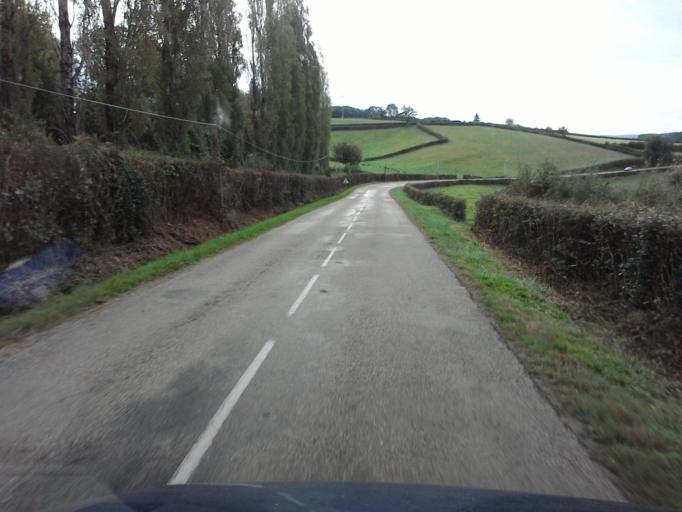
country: FR
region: Bourgogne
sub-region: Departement de la Nievre
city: Lormes
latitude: 47.1974
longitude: 3.8505
